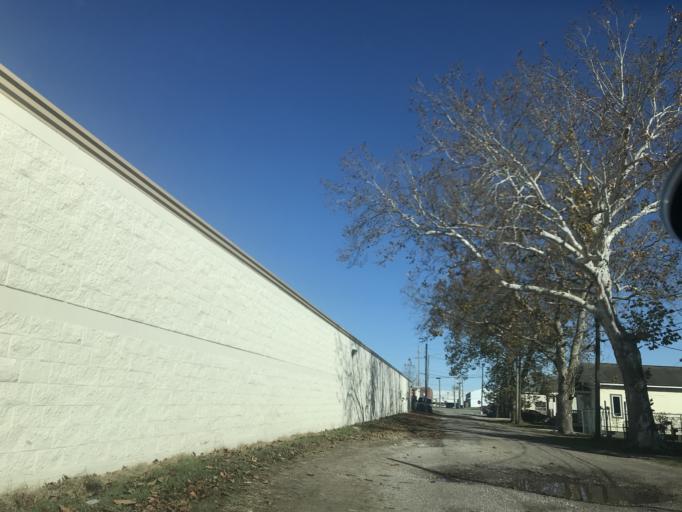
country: US
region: Louisiana
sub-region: Orleans Parish
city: New Orleans
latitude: 29.9564
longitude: -90.1023
